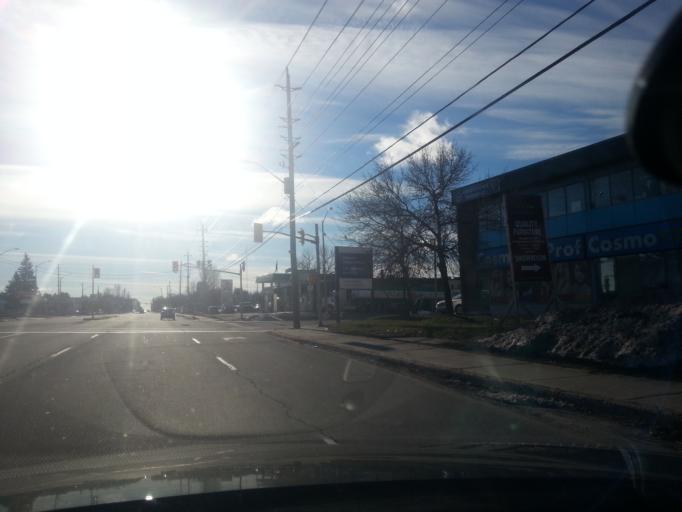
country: CA
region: Ontario
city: Ottawa
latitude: 45.3278
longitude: -75.7202
